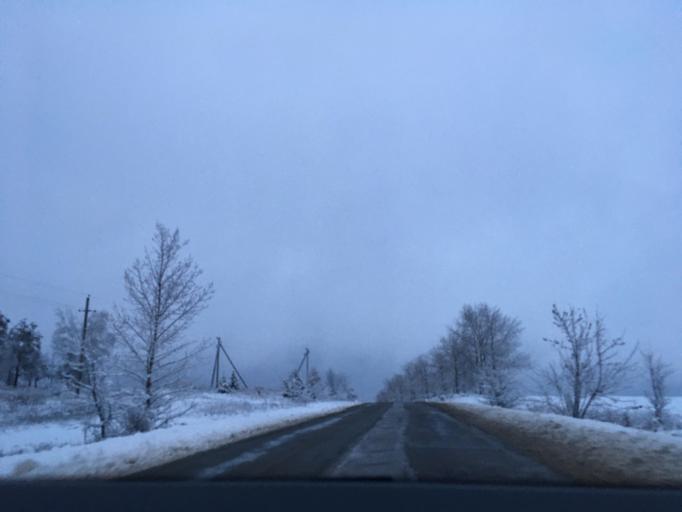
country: RU
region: Voronezj
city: Verkhniy Mamon
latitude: 50.0642
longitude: 40.2782
